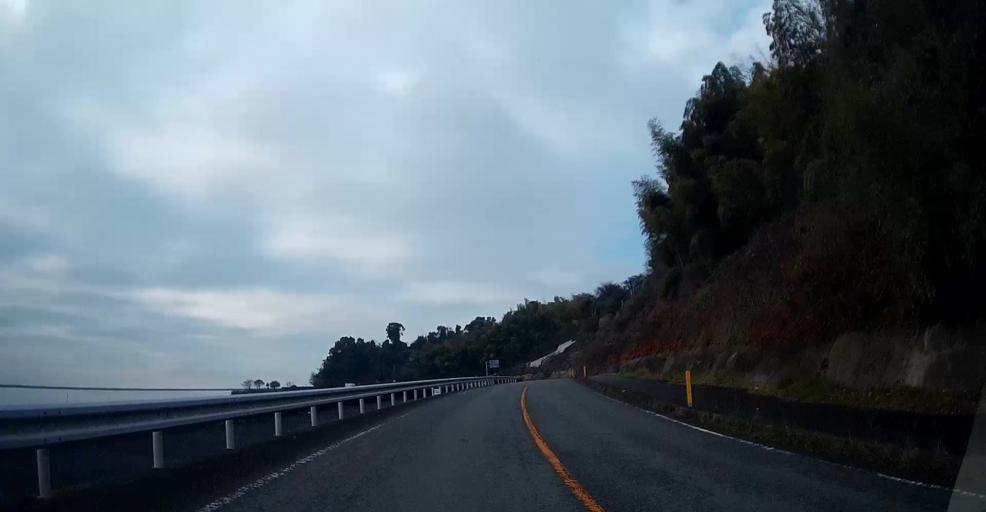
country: JP
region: Kumamoto
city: Matsubase
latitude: 32.6360
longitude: 130.6382
